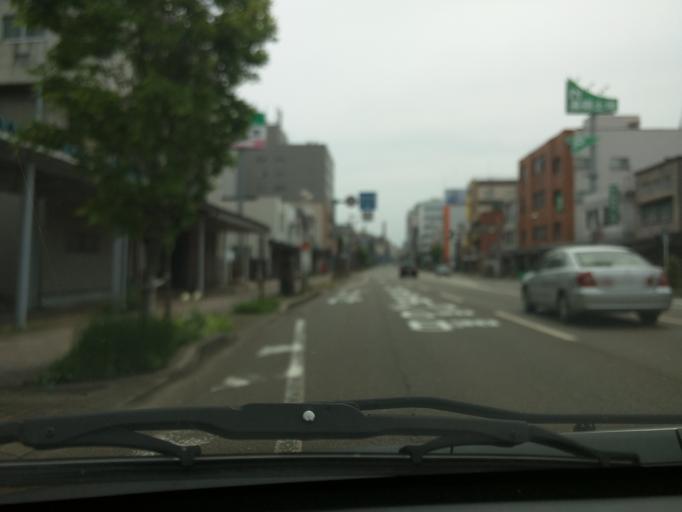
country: JP
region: Niigata
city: Nagaoka
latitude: 37.4517
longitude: 138.8522
